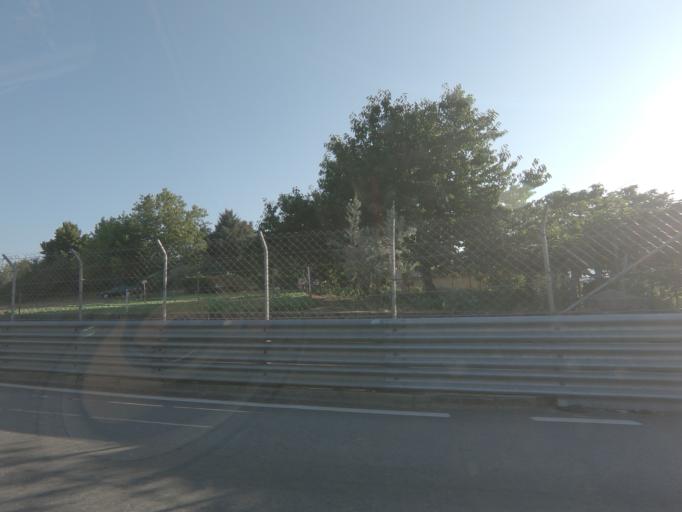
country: PT
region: Vila Real
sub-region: Vila Real
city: Vila Real
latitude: 41.3016
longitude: -7.7167
